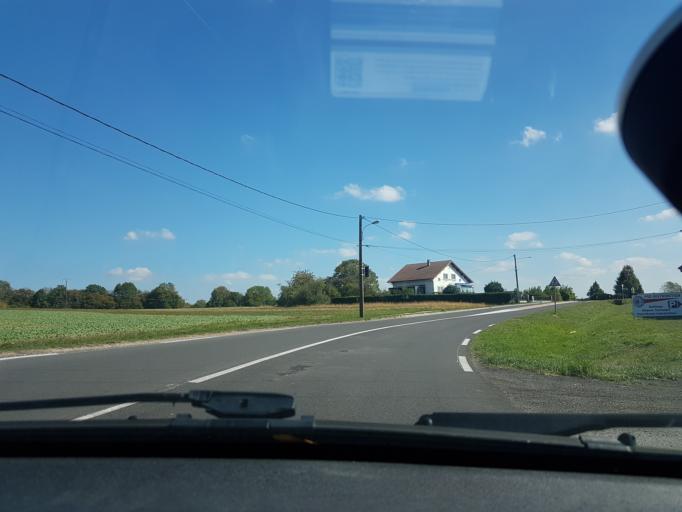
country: FR
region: Franche-Comte
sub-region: Territoire de Belfort
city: Chevremont
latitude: 47.6371
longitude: 6.8957
